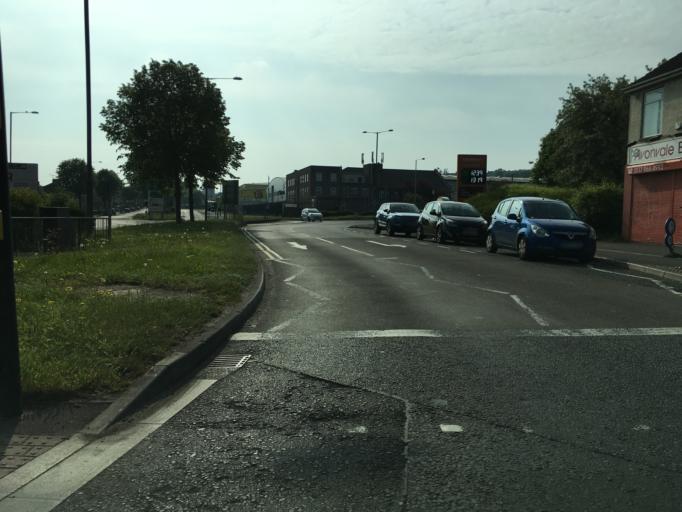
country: GB
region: England
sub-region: Bristol
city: Bristol
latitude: 51.4349
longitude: -2.6186
